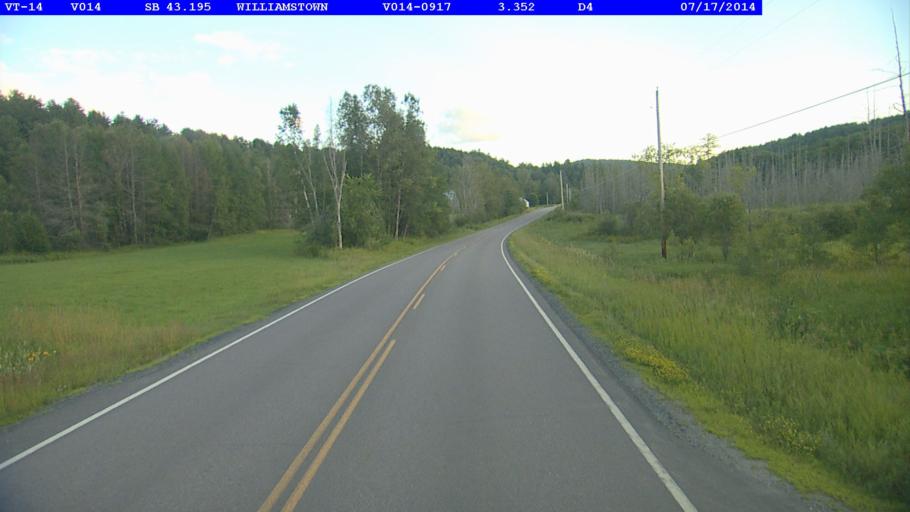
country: US
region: Vermont
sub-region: Orange County
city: Williamstown
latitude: 44.1062
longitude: -72.5418
